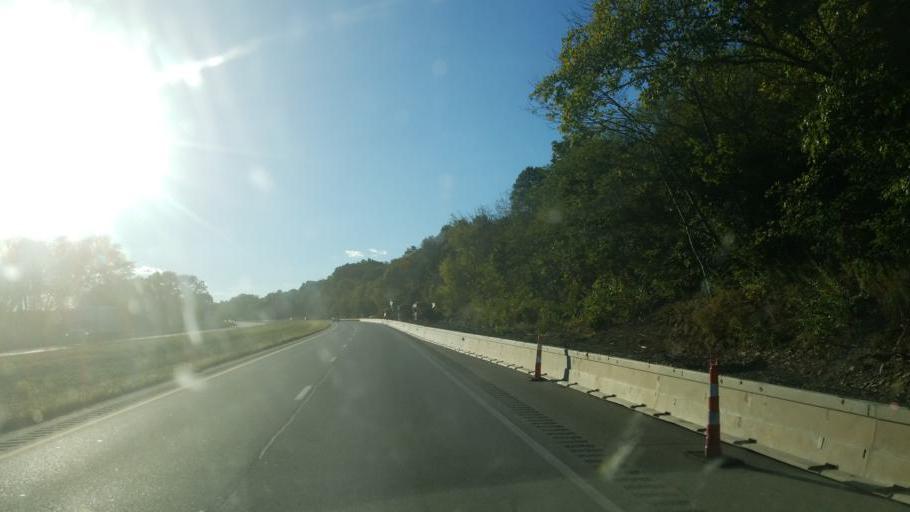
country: US
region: Ohio
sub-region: Guernsey County
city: Byesville
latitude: 40.0046
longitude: -81.5291
